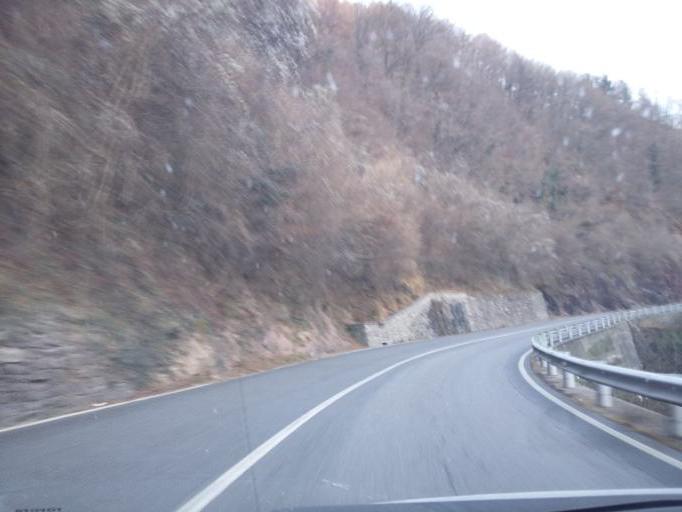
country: IT
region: Lombardy
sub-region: Provincia di Brescia
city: Lavenone
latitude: 45.7353
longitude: 10.4510
